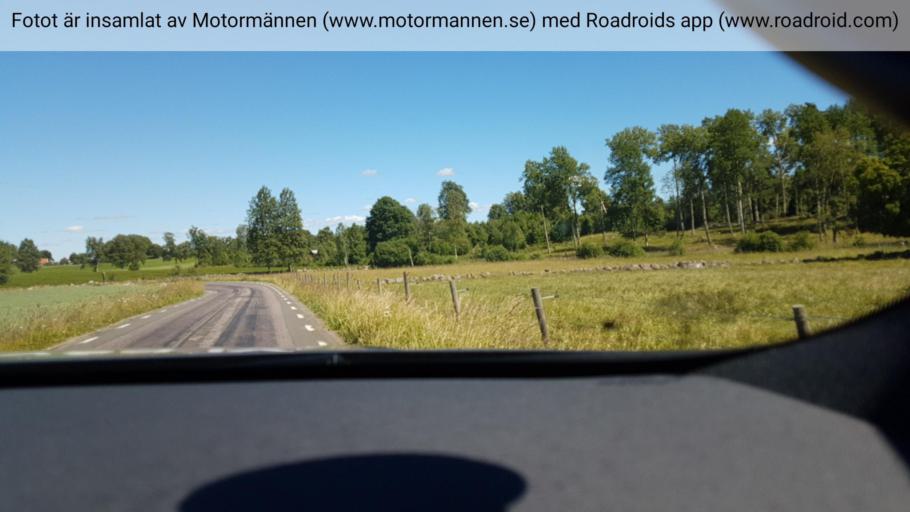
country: SE
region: Vaestra Goetaland
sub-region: Falkopings Kommun
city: Falkoeping
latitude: 58.0701
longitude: 13.5491
